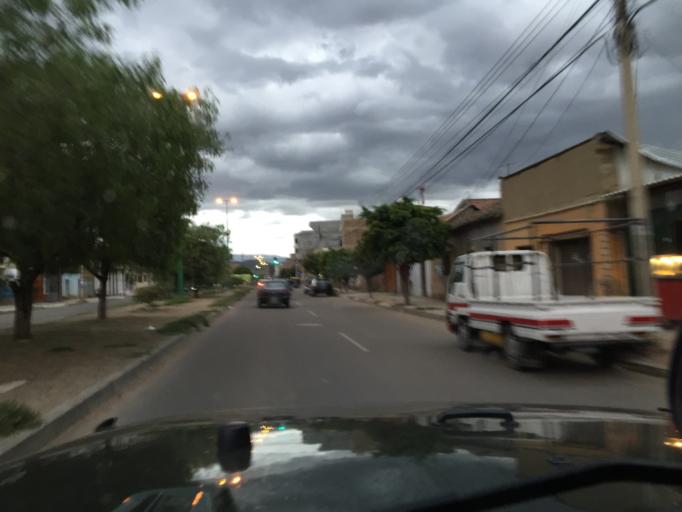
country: BO
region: Cochabamba
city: Cochabamba
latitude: -17.3969
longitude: -66.1932
